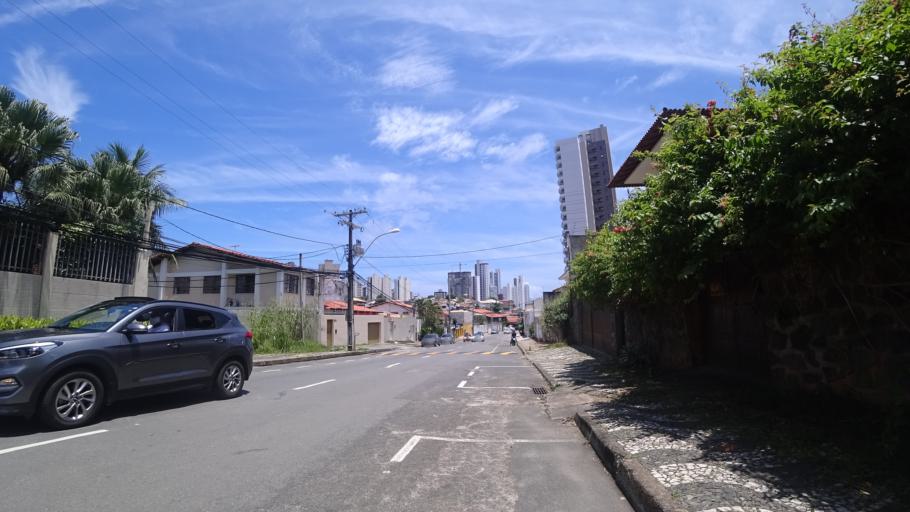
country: BR
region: Bahia
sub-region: Salvador
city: Salvador
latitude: -12.9839
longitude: -38.4590
